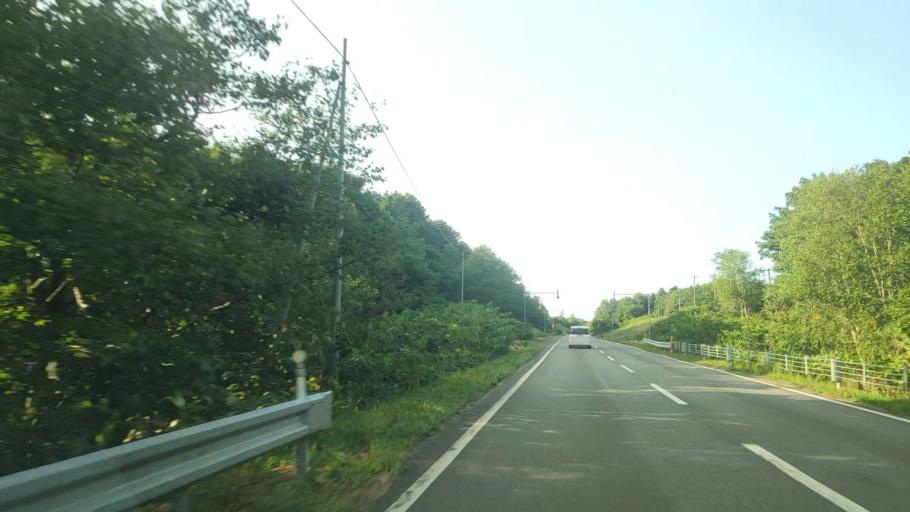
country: JP
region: Hokkaido
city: Makubetsu
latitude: 45.0629
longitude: 141.7483
